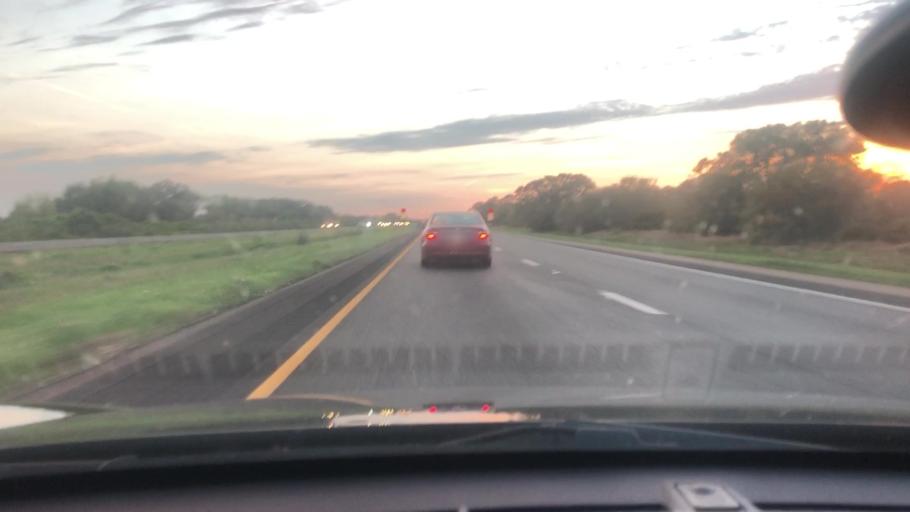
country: US
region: Texas
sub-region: Victoria County
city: Inez
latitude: 28.9191
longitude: -96.7625
